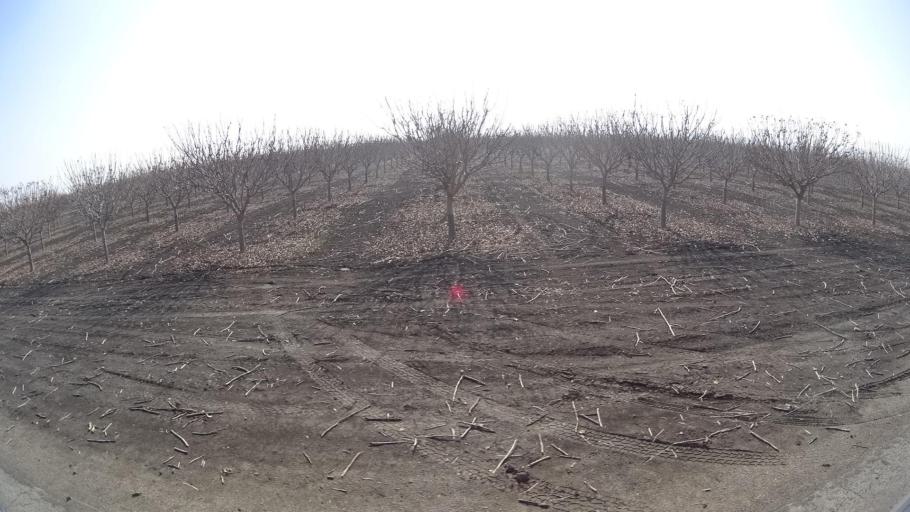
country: US
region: California
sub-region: Kern County
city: Buttonwillow
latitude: 35.3402
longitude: -119.4043
